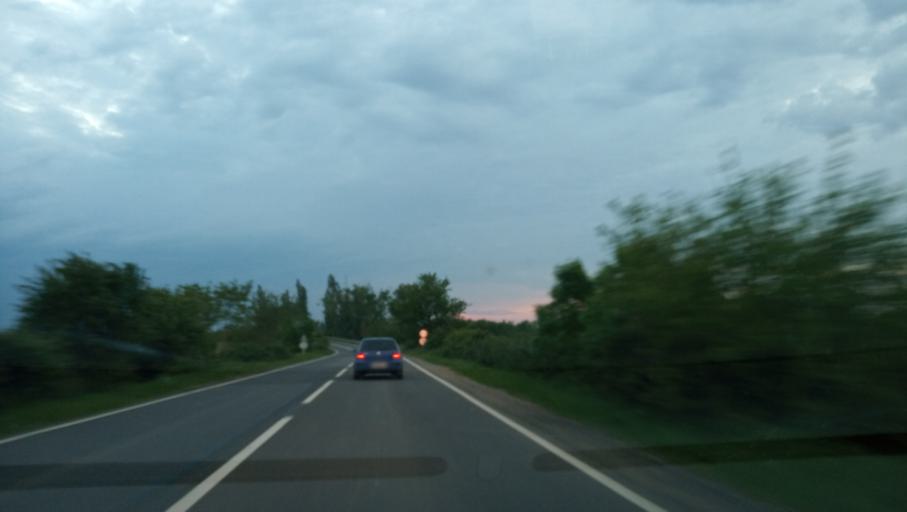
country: RO
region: Timis
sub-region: Comuna Sag
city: Sag
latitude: 45.6351
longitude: 21.1857
